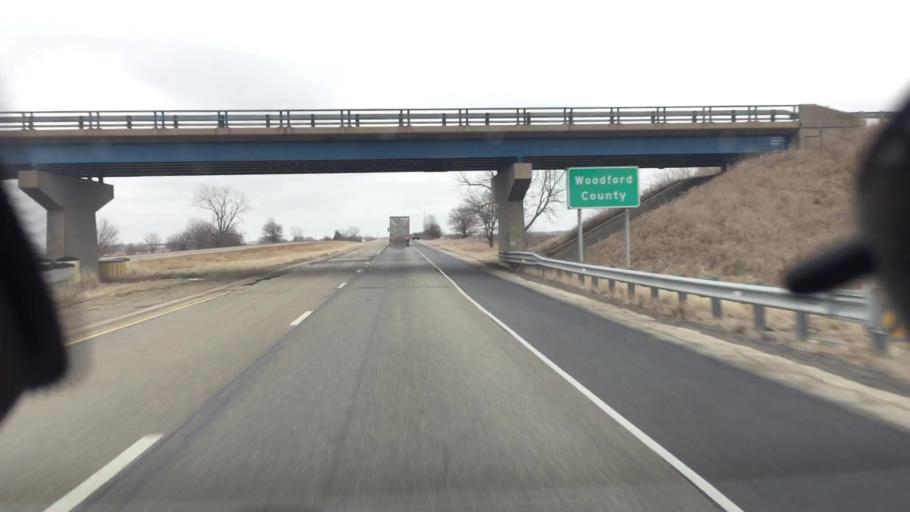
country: US
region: Illinois
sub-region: Tazewell County
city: Mackinaw
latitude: 40.6224
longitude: -89.3279
